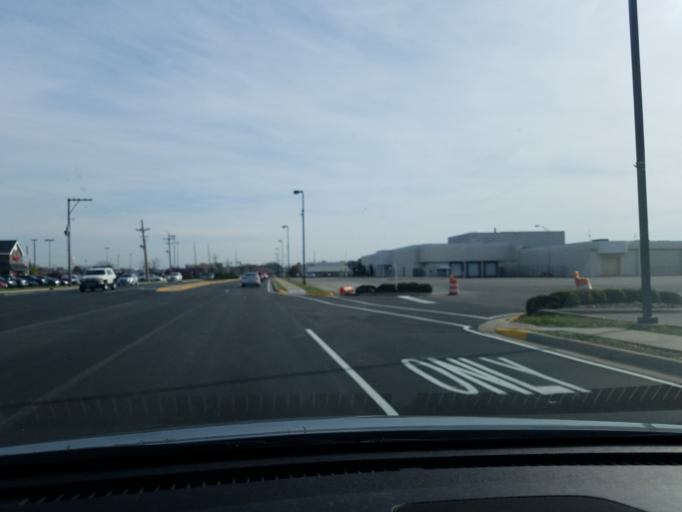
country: US
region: Indiana
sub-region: Clark County
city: Clarksville
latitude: 38.3178
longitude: -85.7631
